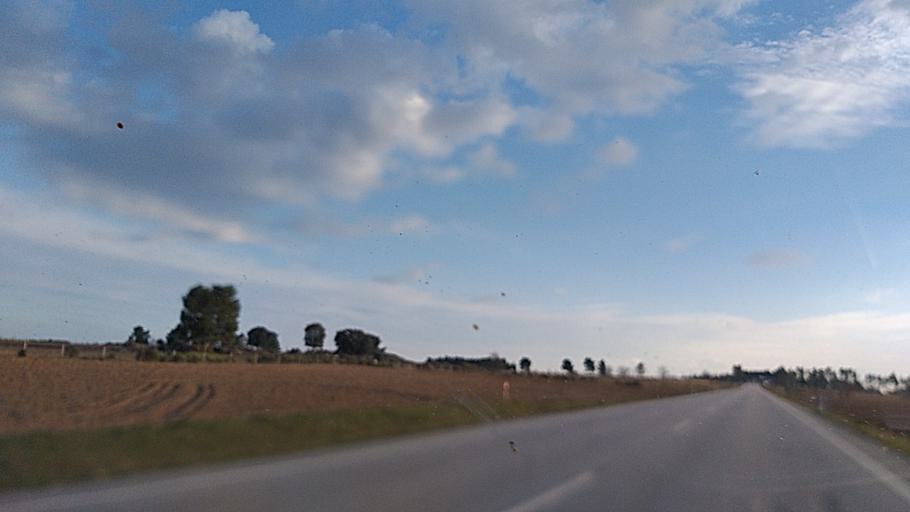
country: PT
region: Guarda
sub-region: Pinhel
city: Pinhel
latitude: 40.6495
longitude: -6.9676
